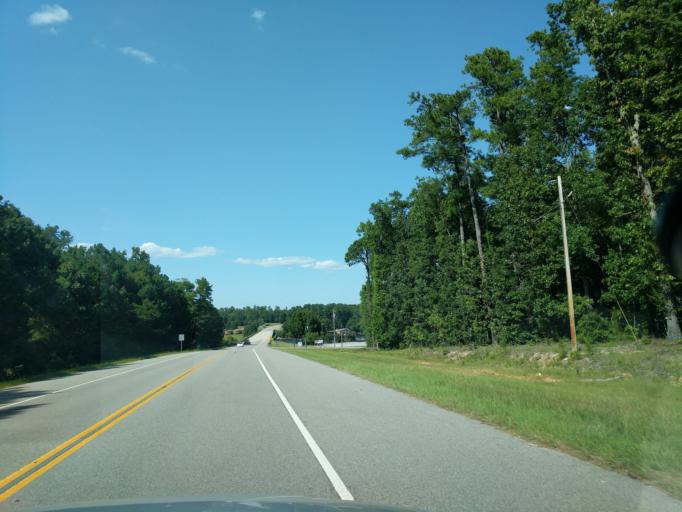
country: US
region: South Carolina
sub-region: Newberry County
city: Prosperity
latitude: 34.0964
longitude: -81.5687
